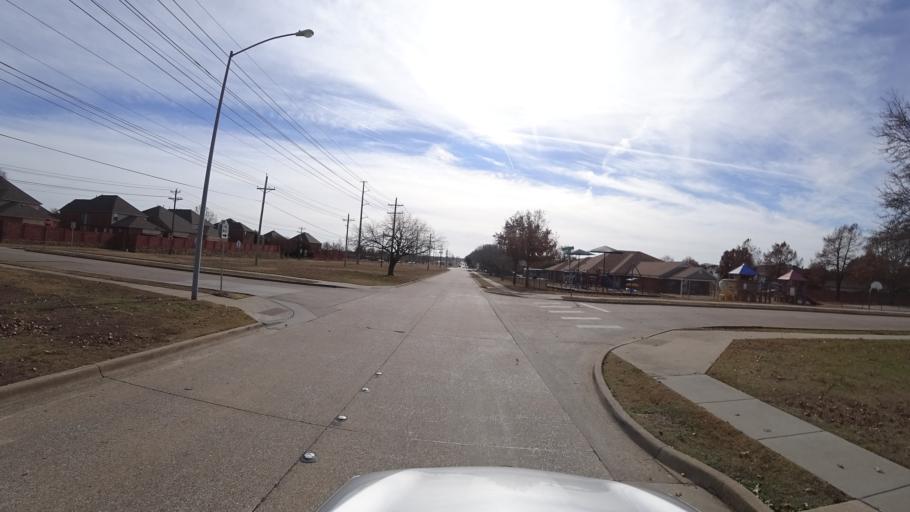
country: US
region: Texas
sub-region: Denton County
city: Highland Village
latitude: 33.0660
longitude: -97.0359
